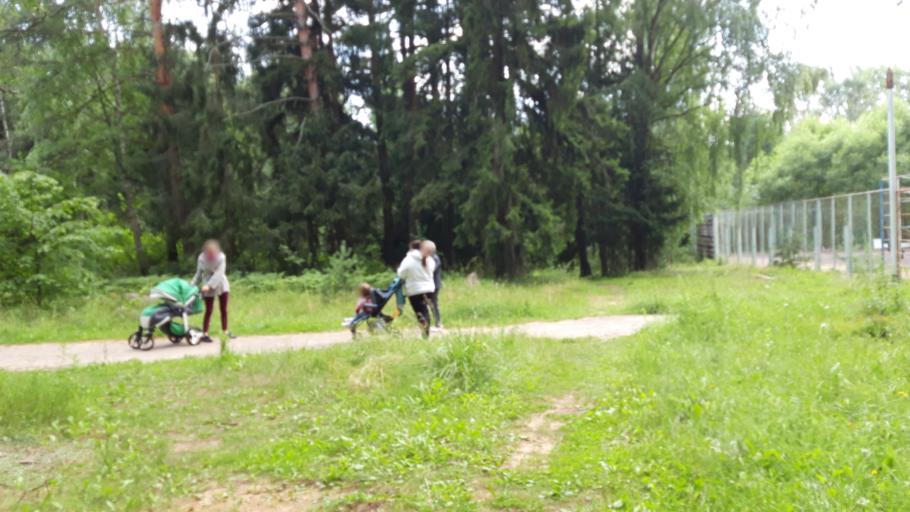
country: RU
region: Tverskaya
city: Konakovo
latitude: 56.6706
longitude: 36.6846
